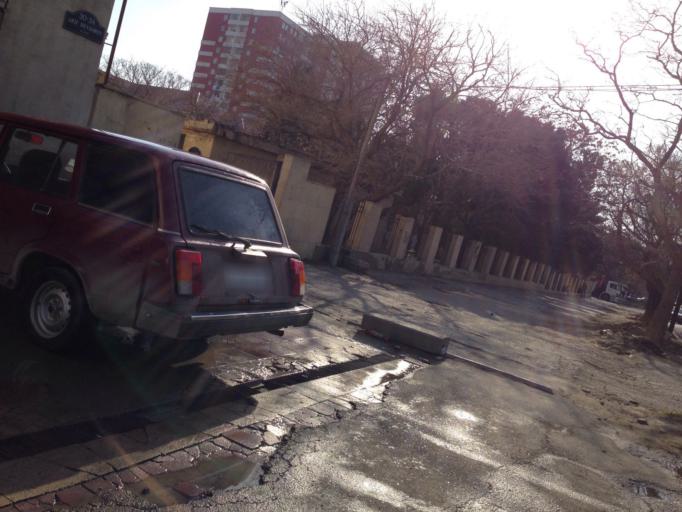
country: AZ
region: Baki
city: Baku
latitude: 40.3962
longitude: 49.8741
